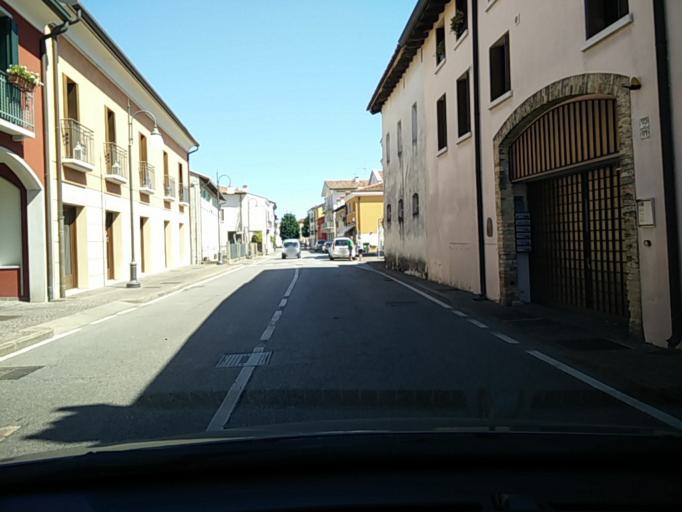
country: IT
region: Veneto
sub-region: Provincia di Venezia
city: Concordia Sagittaria
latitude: 45.7572
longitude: 12.8426
